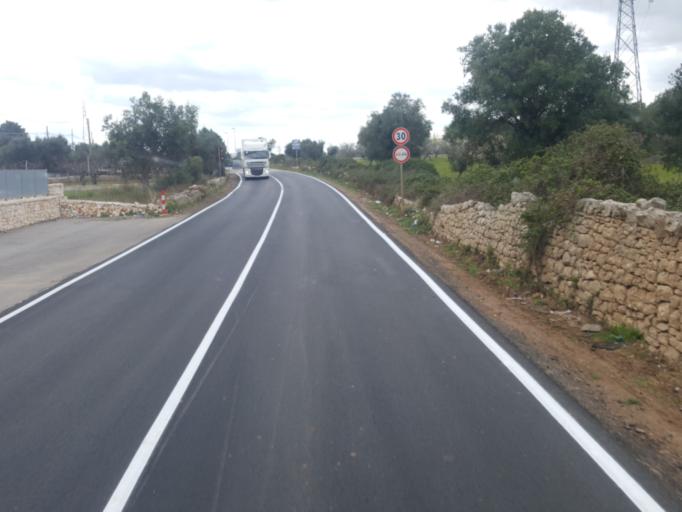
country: IT
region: Apulia
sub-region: Provincia di Bari
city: Conversano
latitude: 40.9848
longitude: 17.1208
